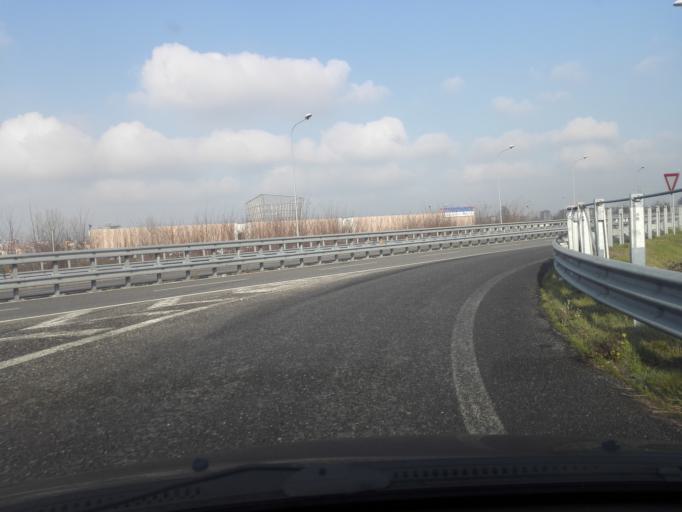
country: IT
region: Piedmont
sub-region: Provincia di Alessandria
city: Alessandria
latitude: 44.8991
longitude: 8.6343
